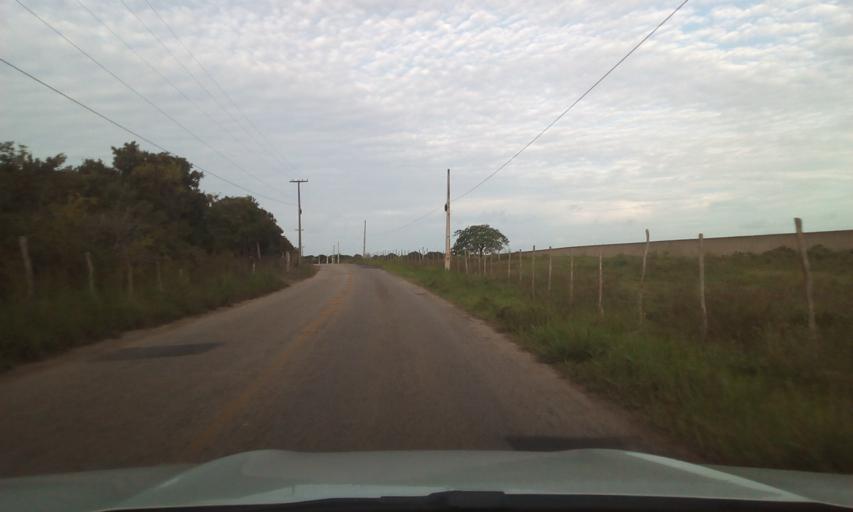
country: BR
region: Paraiba
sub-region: Conde
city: Conde
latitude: -7.2241
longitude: -34.8224
